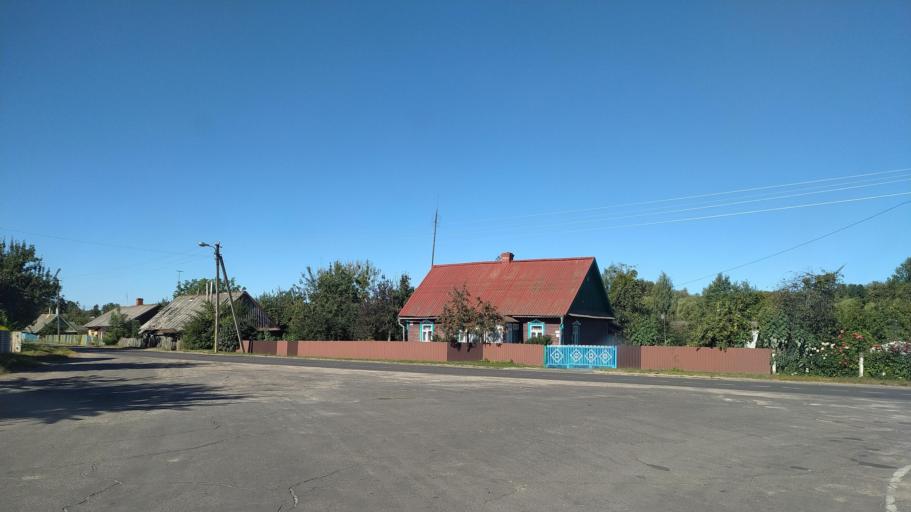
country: BY
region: Brest
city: Pruzhany
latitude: 52.4846
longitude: 24.7074
